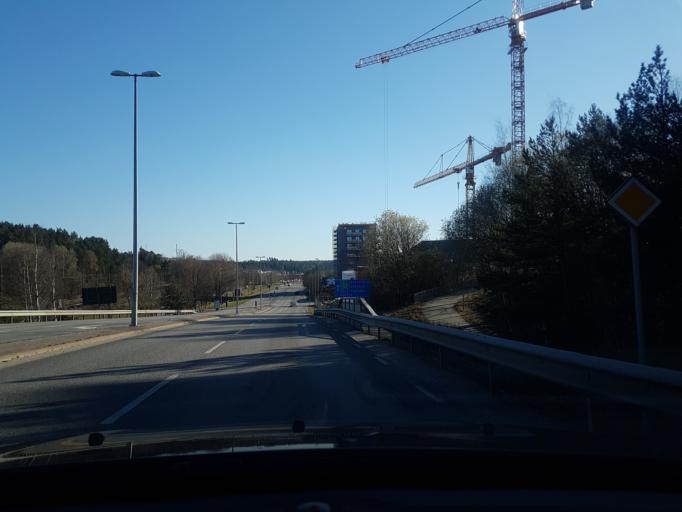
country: SE
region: Stockholm
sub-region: Sigtuna Kommun
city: Marsta
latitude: 59.6232
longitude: 17.8599
